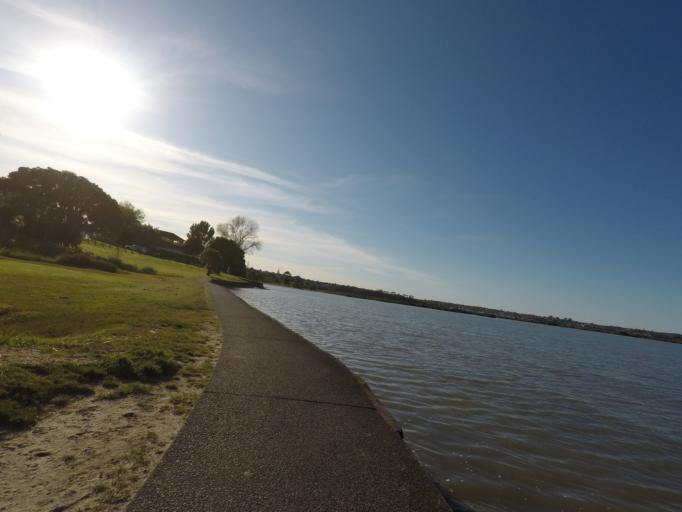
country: NZ
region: Auckland
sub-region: Auckland
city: Rosebank
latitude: -36.8290
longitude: 174.6572
